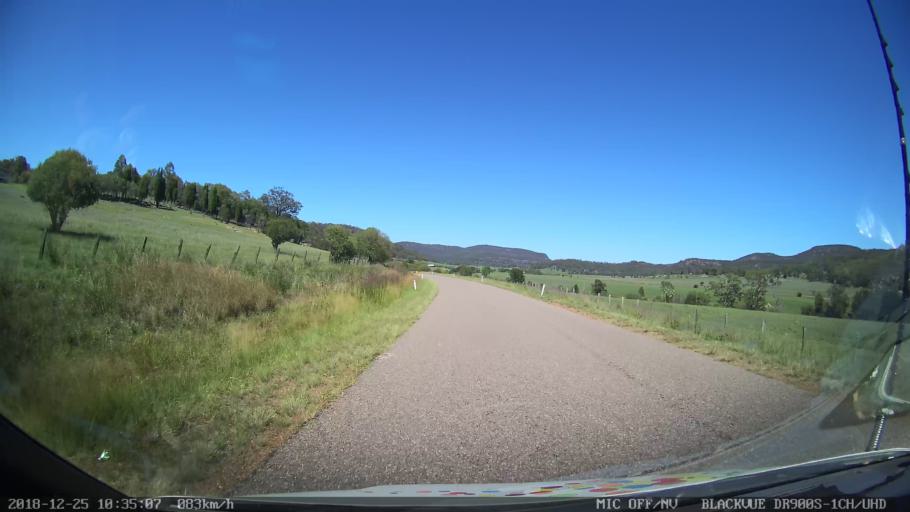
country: AU
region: New South Wales
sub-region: Upper Hunter Shire
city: Merriwa
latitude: -32.3956
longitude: 150.3991
